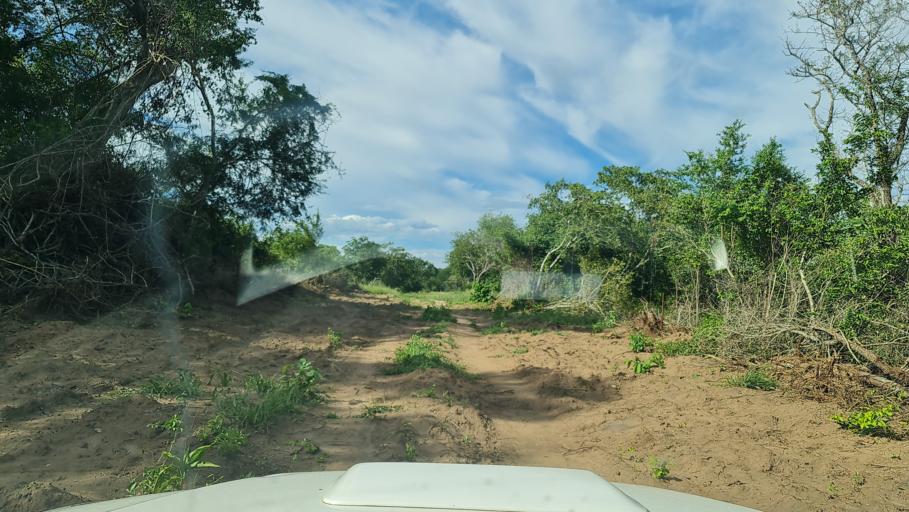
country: MZ
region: Nampula
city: Ilha de Mocambique
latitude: -15.5026
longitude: 40.1578
